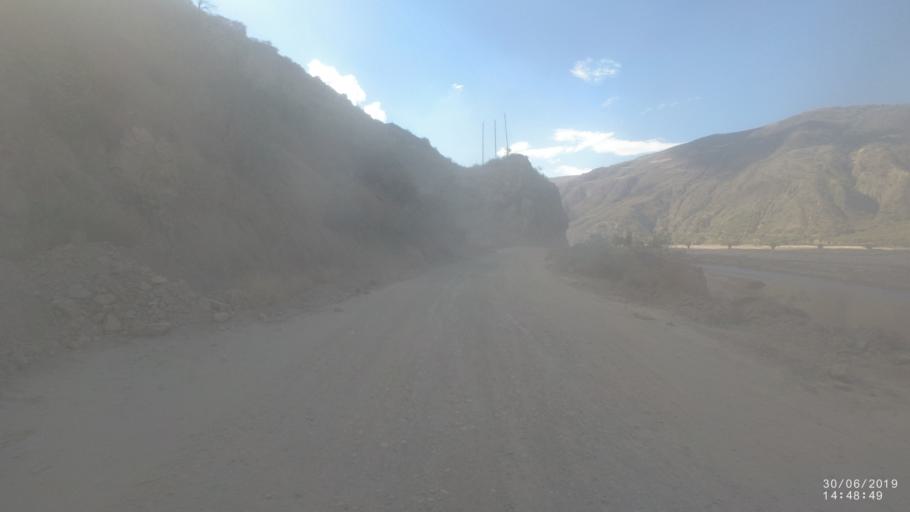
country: BO
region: Cochabamba
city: Irpa Irpa
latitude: -17.7869
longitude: -66.3420
